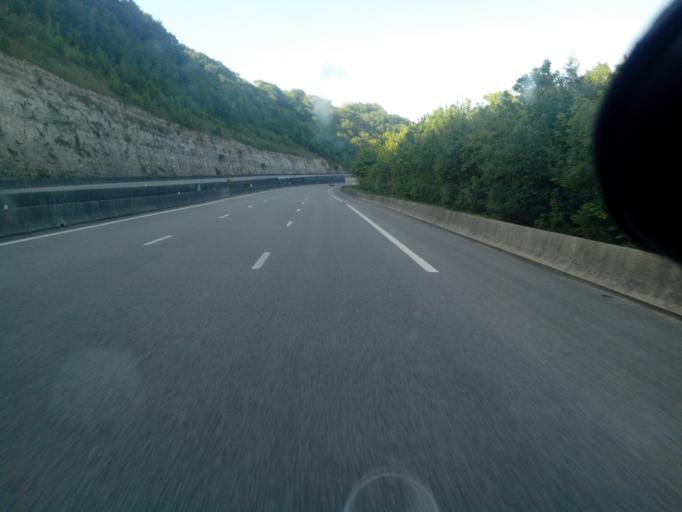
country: FR
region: Haute-Normandie
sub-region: Departement de la Seine-Maritime
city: Rogerville
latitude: 49.5028
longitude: 0.2787
